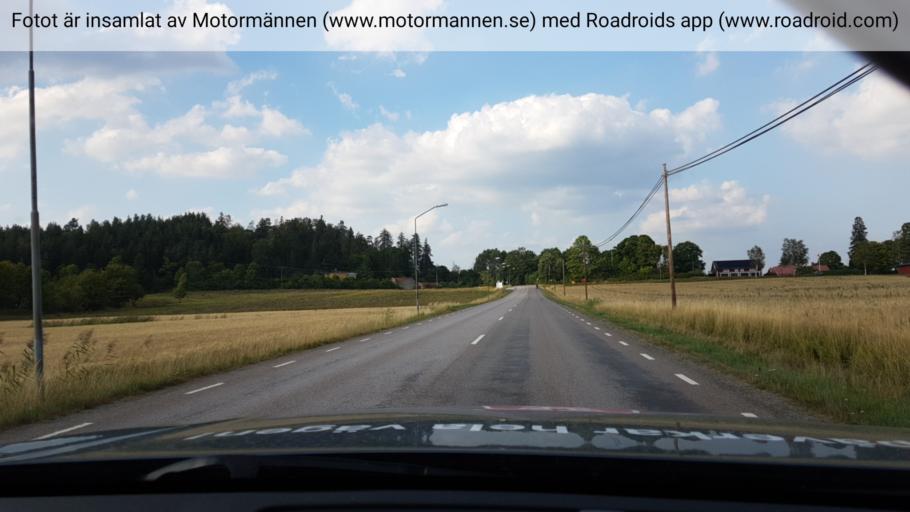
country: SE
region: Soedermanland
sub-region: Gnesta Kommun
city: Gnesta
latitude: 59.0559
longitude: 17.3042
